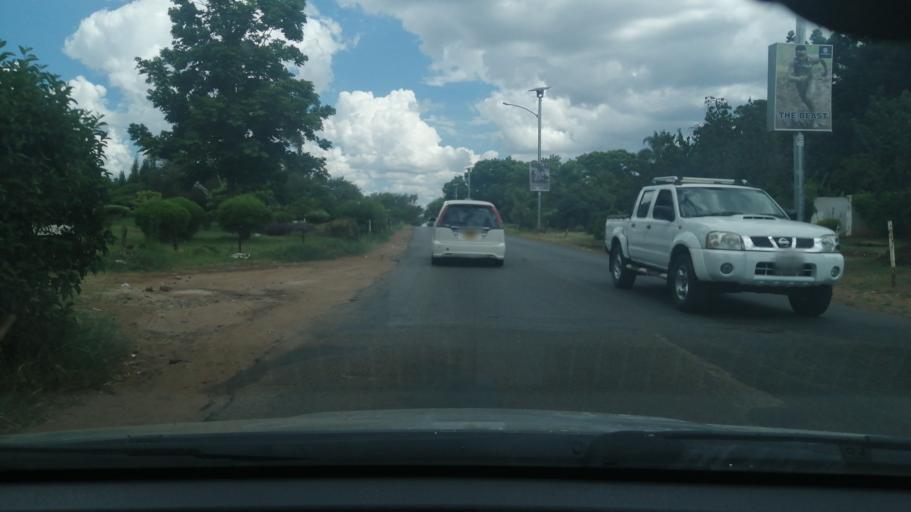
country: ZW
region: Harare
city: Harare
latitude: -17.7922
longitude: 31.0664
